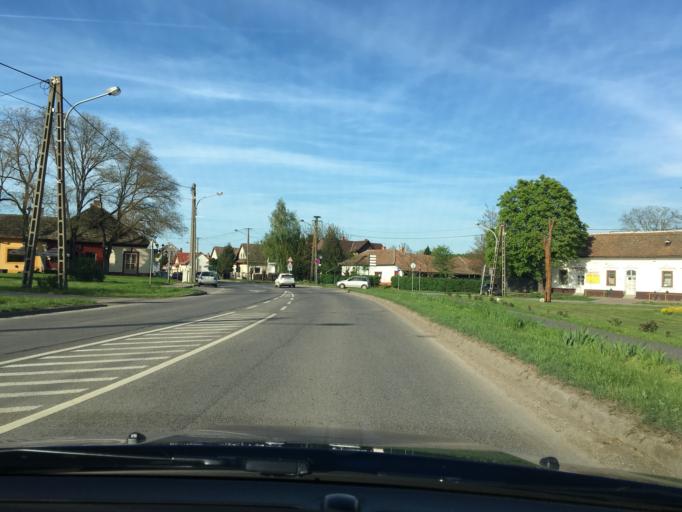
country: HU
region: Bekes
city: Korosladany
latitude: 46.9595
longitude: 21.0837
